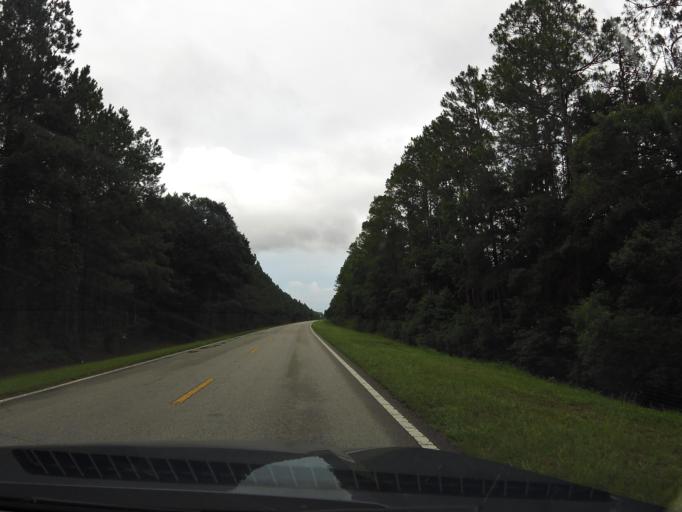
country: US
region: Florida
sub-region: Saint Johns County
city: Saint Augustine South
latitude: 29.8554
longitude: -81.4595
